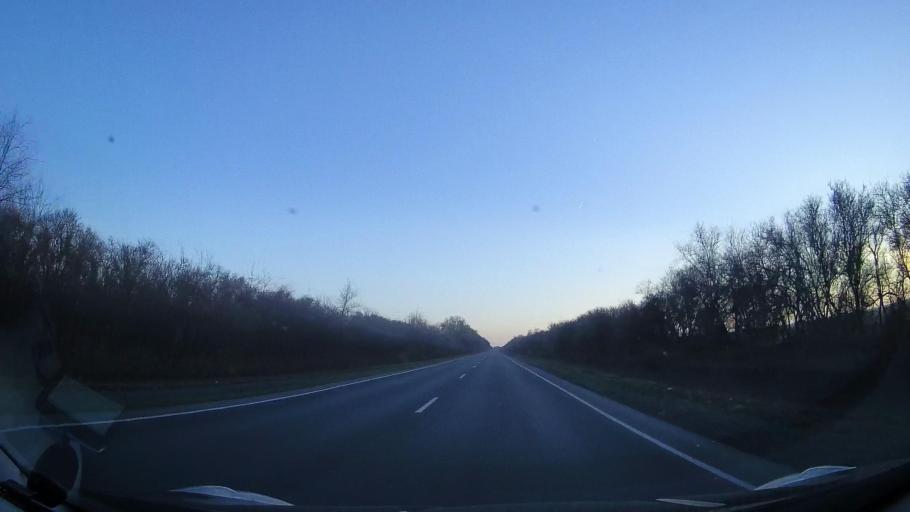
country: RU
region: Rostov
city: Bagayevskaya
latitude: 47.1323
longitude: 40.2766
